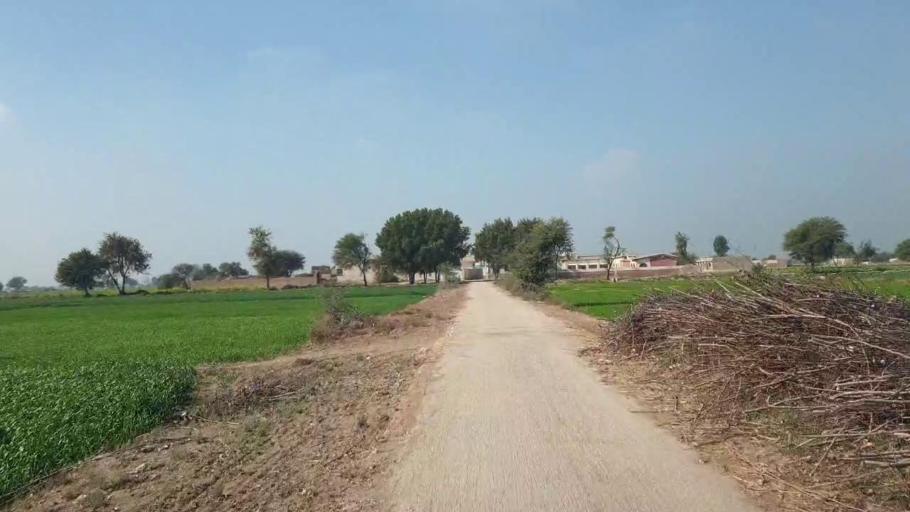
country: PK
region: Sindh
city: Shahdadpur
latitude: 26.0209
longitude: 68.5917
